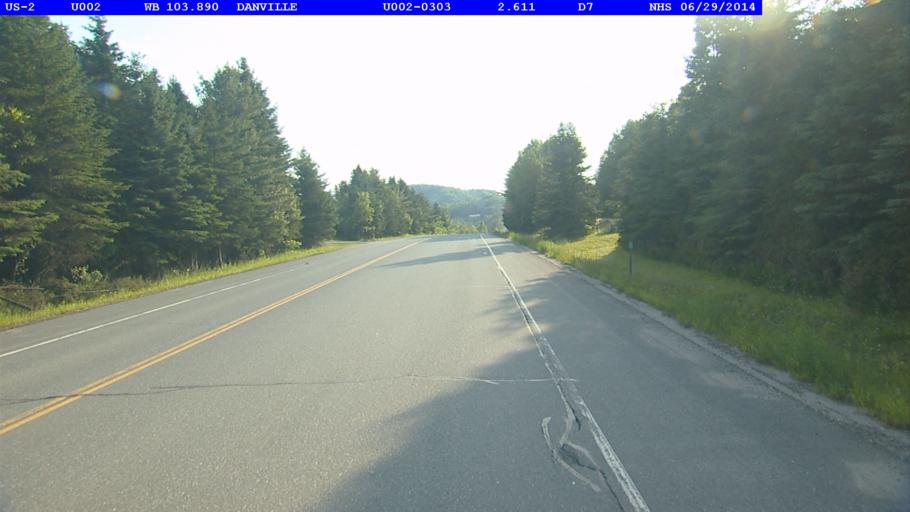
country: US
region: Vermont
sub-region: Caledonia County
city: Saint Johnsbury
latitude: 44.4097
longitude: -72.1771
